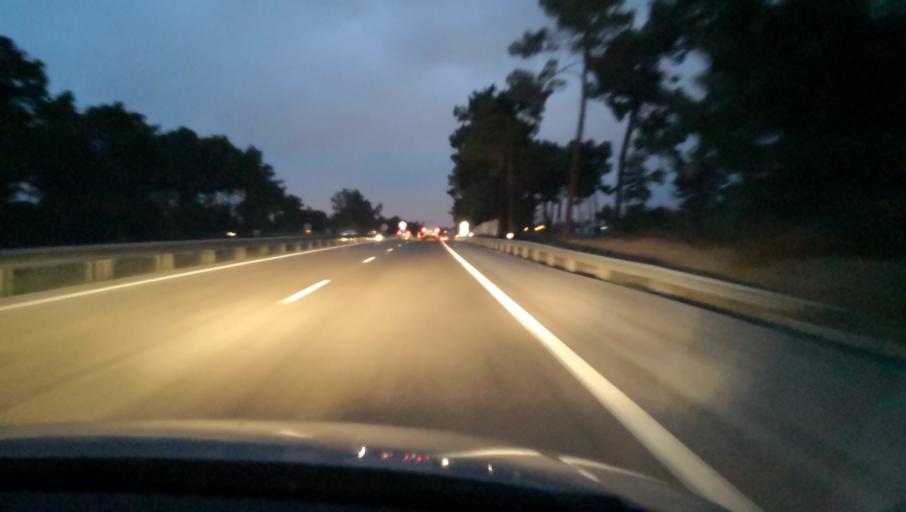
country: PT
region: Setubal
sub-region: Barreiro
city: Santo Antonio da Charneca
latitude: 38.6100
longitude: -9.0246
